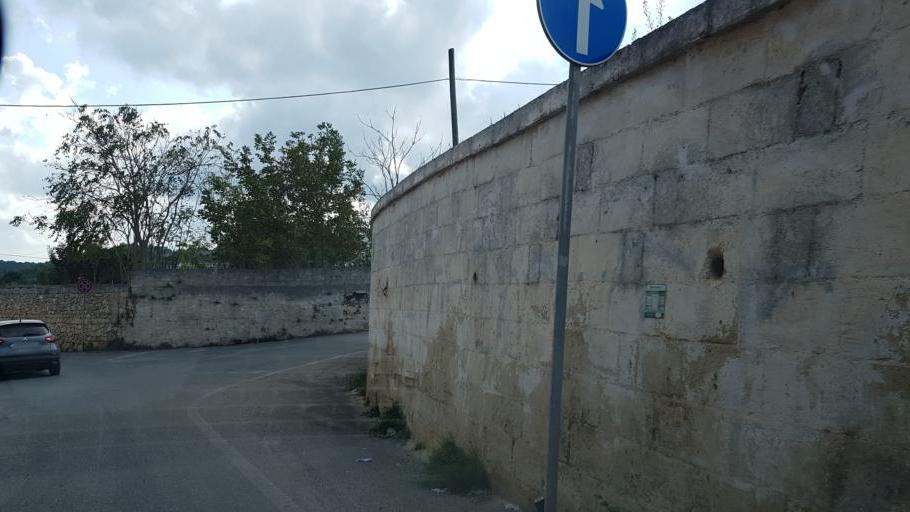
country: IT
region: Apulia
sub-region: Provincia di Brindisi
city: Ostuni
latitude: 40.7340
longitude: 17.5815
